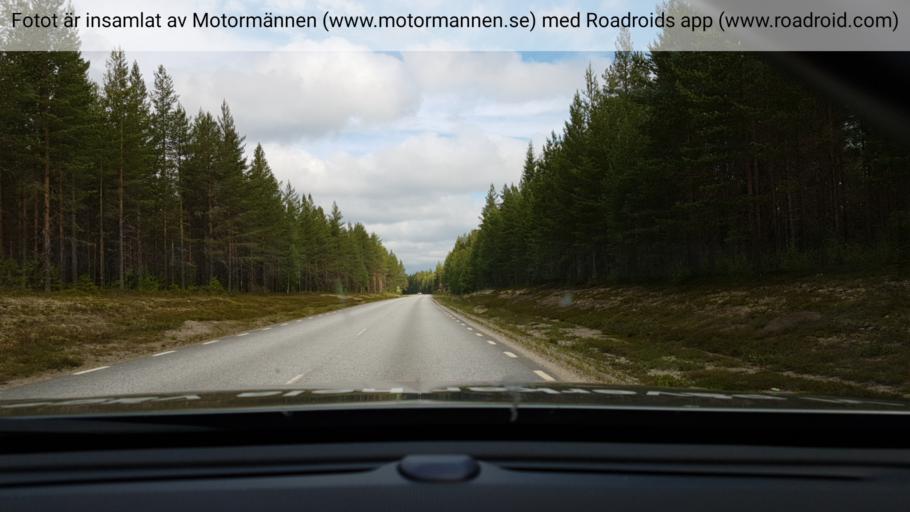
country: SE
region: Vaesterbotten
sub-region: Vindelns Kommun
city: Vindeln
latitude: 64.3668
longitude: 19.4318
